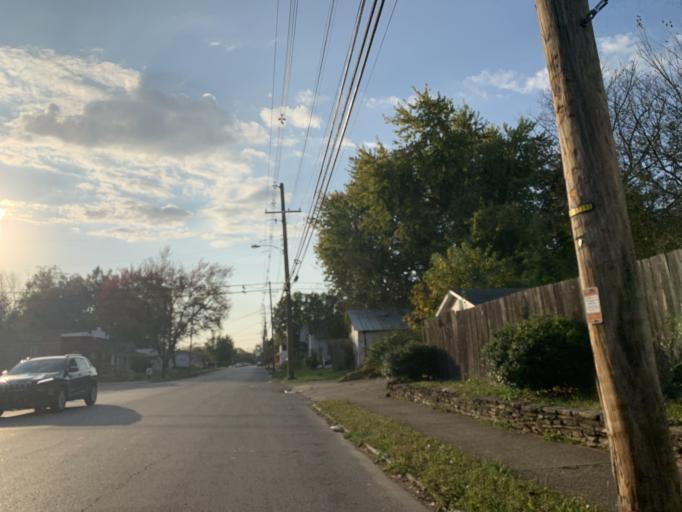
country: US
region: Kentucky
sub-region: Jefferson County
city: Shively
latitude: 38.2321
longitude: -85.8054
